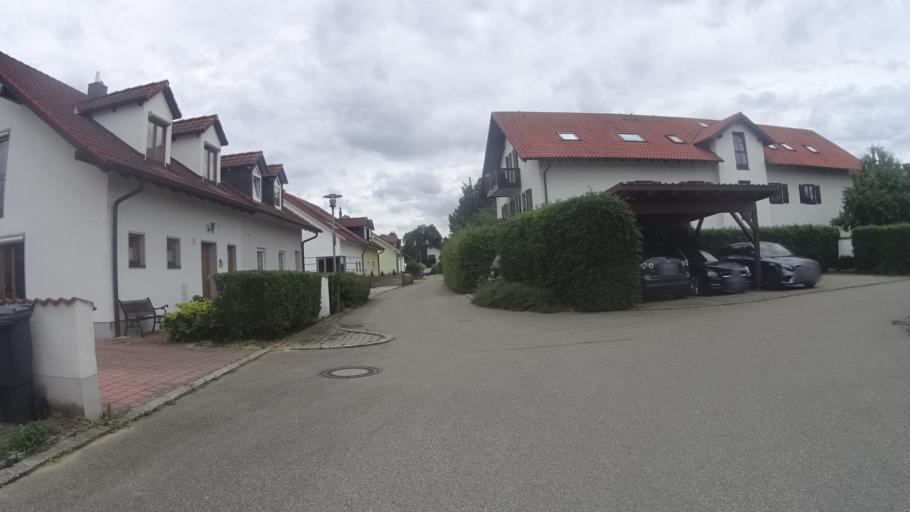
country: DE
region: Bavaria
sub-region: Upper Bavaria
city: Stammham
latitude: 48.3080
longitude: 11.8699
